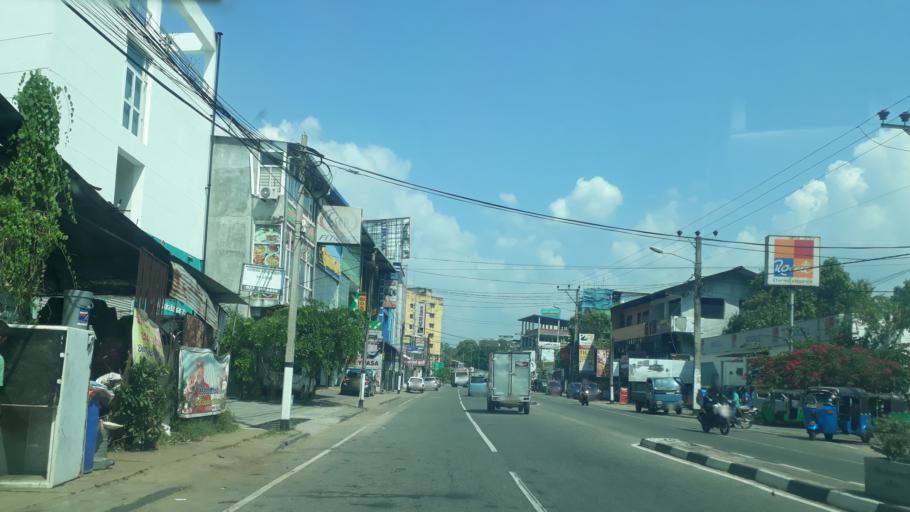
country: LK
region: Western
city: Gampaha
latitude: 7.0912
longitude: 79.9979
